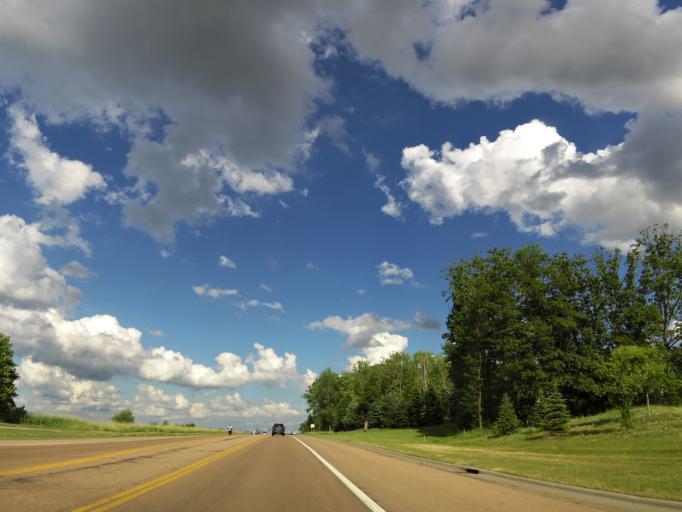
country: US
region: Minnesota
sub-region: Carver County
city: Waconia
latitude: 44.8364
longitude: -93.7788
